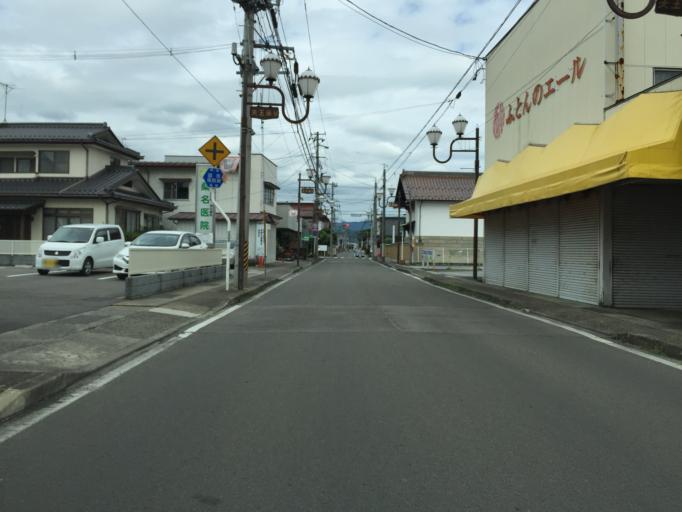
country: JP
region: Fukushima
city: Hobaramachi
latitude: 37.8197
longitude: 140.5019
